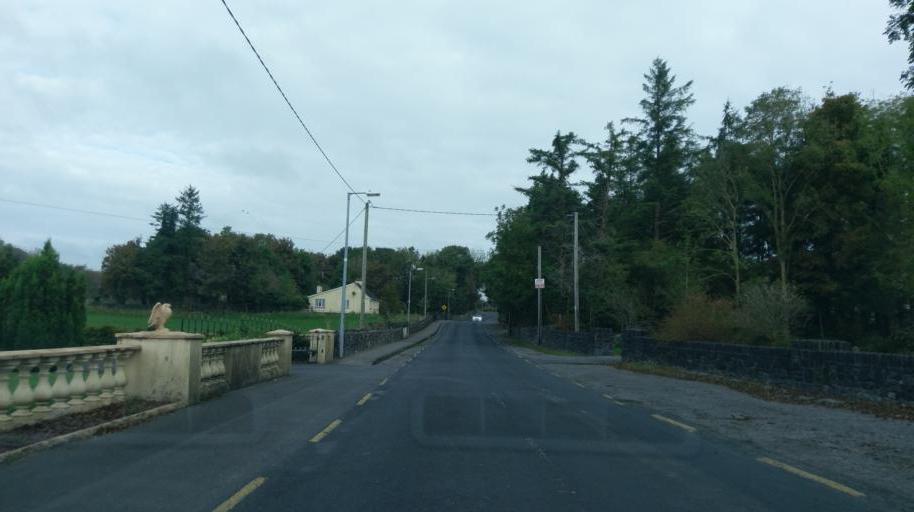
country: IE
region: Connaught
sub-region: County Galway
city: Athenry
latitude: 53.3717
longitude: -8.7013
